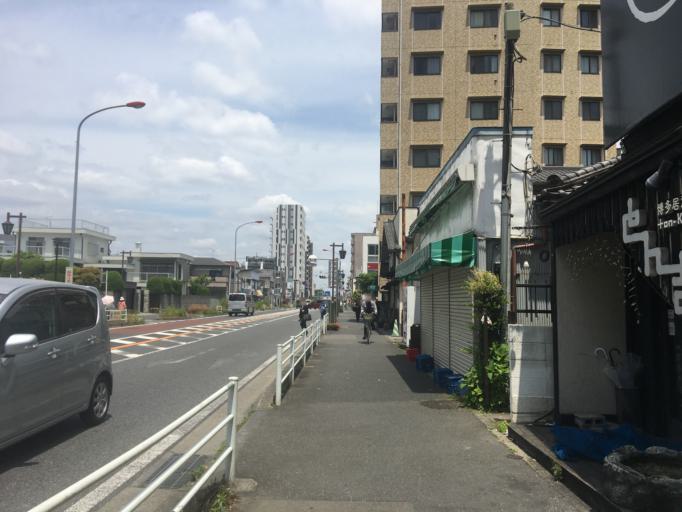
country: JP
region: Saitama
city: Shimotoda
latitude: 35.8128
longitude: 139.6825
